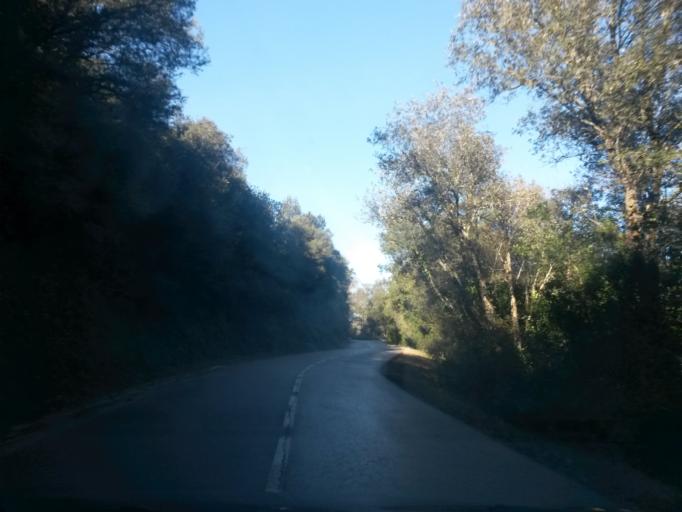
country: ES
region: Catalonia
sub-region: Provincia de Girona
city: Sant Gregori
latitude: 41.9918
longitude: 2.6797
